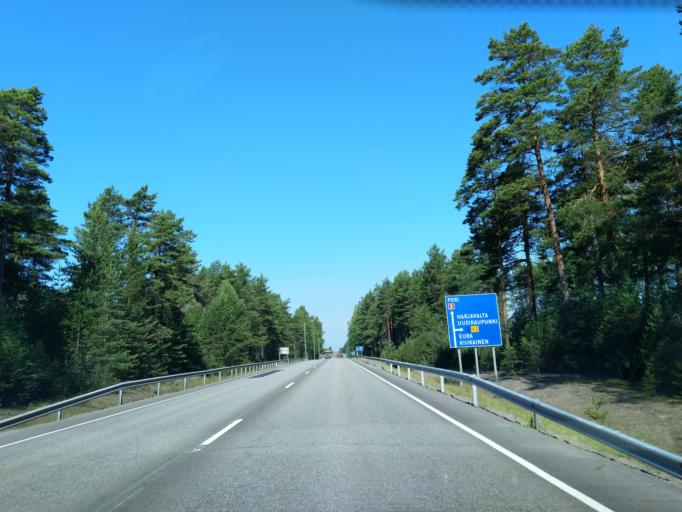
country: FI
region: Satakunta
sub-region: Pori
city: Harjavalta
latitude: 61.3025
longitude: 22.1389
